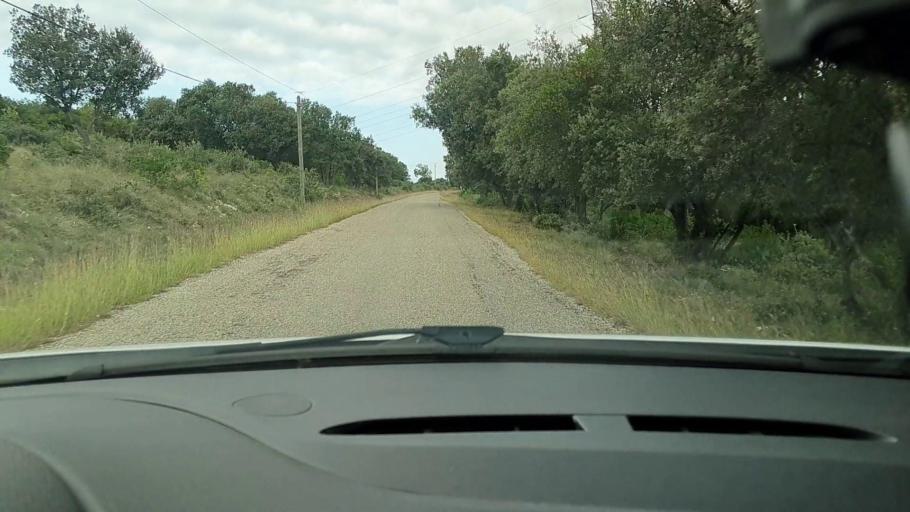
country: FR
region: Languedoc-Roussillon
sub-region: Departement du Gard
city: Montaren-et-Saint-Mediers
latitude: 44.0822
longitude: 4.3004
